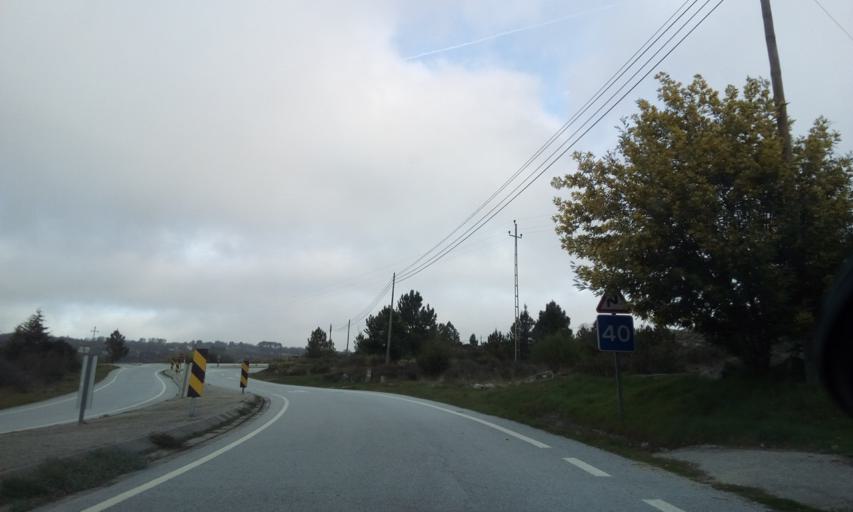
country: PT
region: Guarda
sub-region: Fornos de Algodres
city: Fornos de Algodres
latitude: 40.6575
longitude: -7.4847
